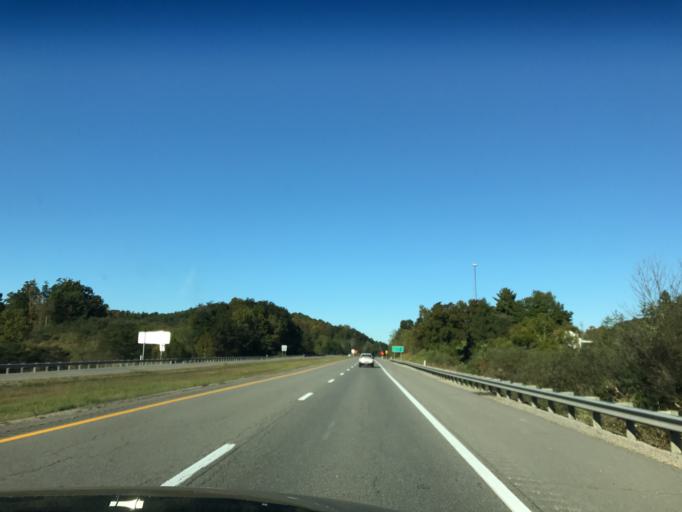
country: US
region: Ohio
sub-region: Washington County
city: Reno
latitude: 39.2515
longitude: -81.3285
